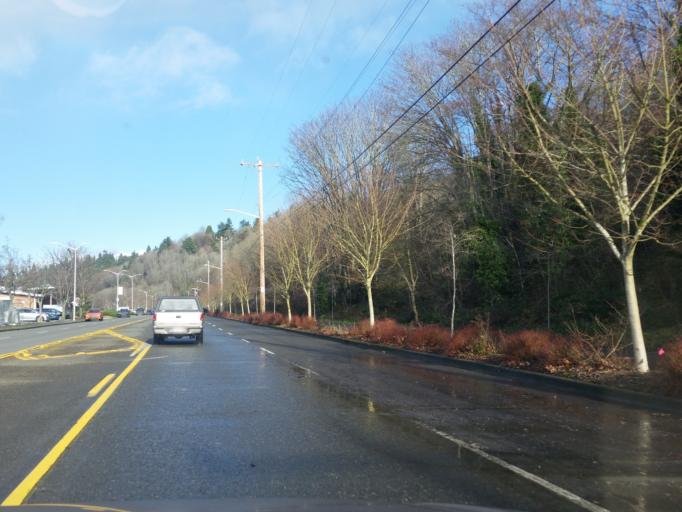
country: US
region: Washington
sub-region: King County
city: Shoreline
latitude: 47.6791
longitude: -122.4053
